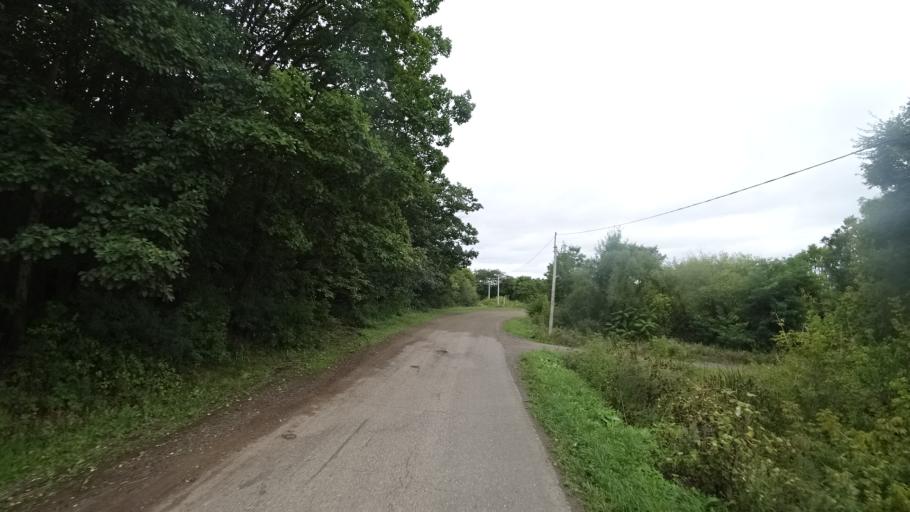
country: RU
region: Primorskiy
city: Chernigovka
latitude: 44.4535
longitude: 132.5852
